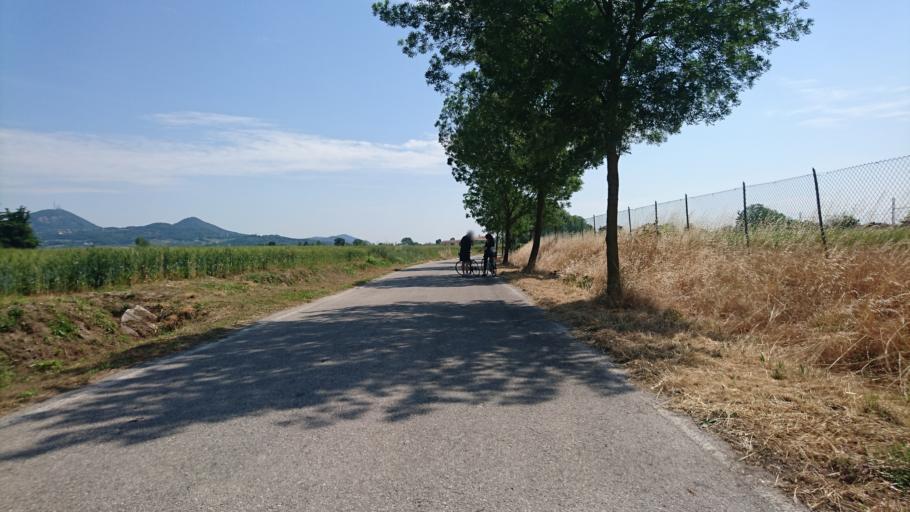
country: IT
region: Veneto
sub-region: Provincia di Padova
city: Ospedaletto Euganeo
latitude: 45.2217
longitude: 11.6185
